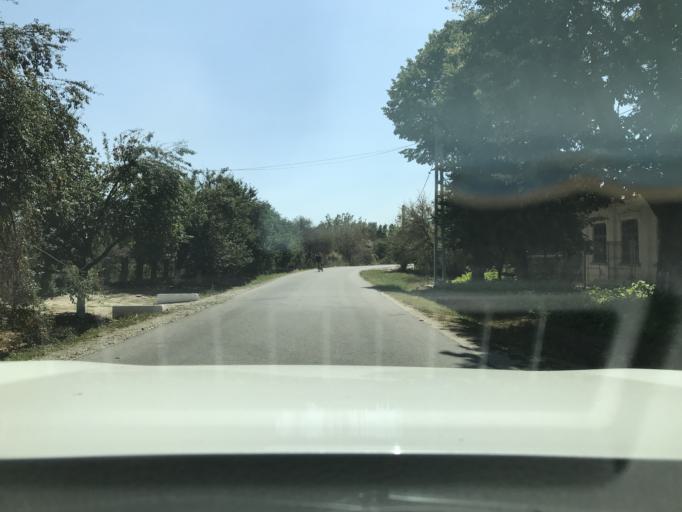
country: RO
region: Olt
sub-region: Comuna Falcoiu
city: Falcoiu
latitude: 44.2386
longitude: 24.3666
